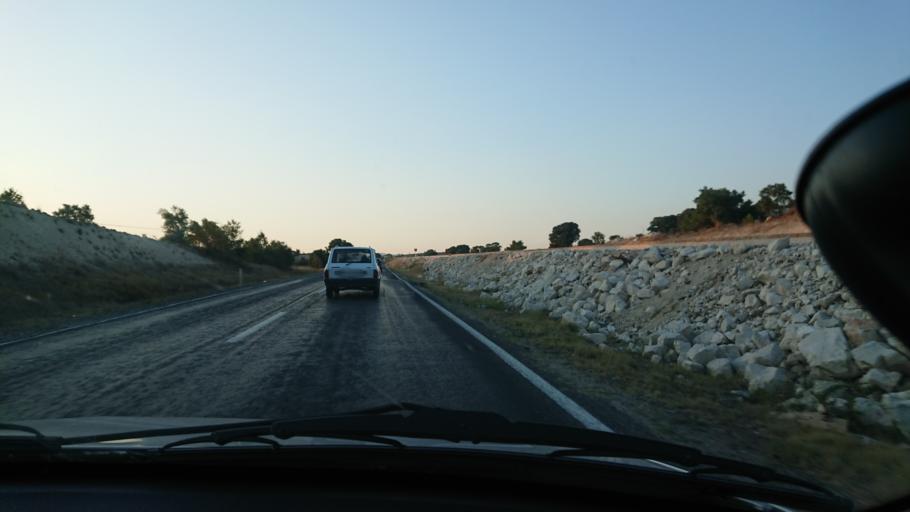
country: TR
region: Usak
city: Gure
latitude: 38.7182
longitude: 29.2063
